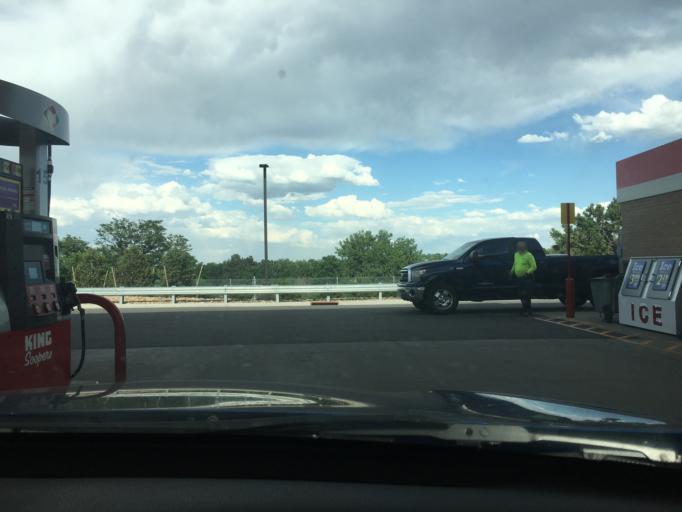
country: US
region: Colorado
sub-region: Jefferson County
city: Applewood
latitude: 39.7626
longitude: -105.1400
